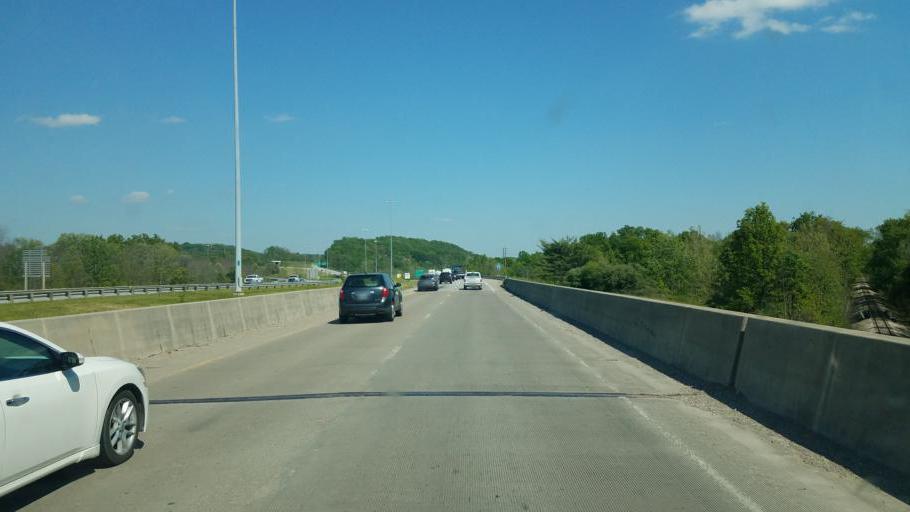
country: US
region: Ohio
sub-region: Guernsey County
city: Cambridge
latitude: 39.9977
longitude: -81.5723
